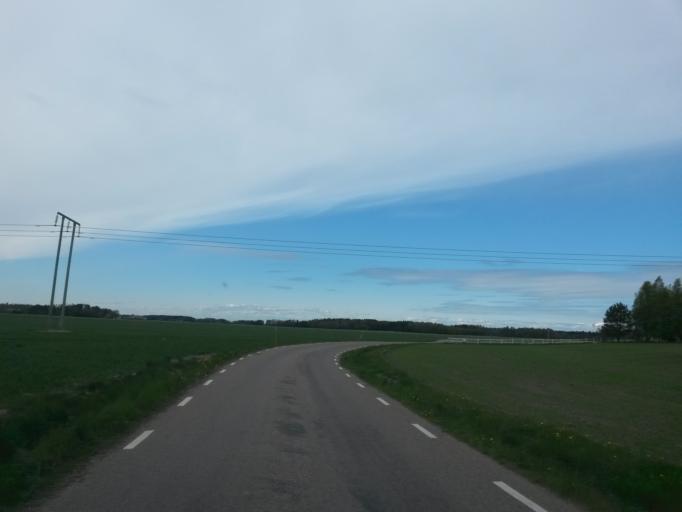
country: SE
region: Vaestra Goetaland
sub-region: Grastorps Kommun
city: Graestorp
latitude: 58.3864
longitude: 12.7895
